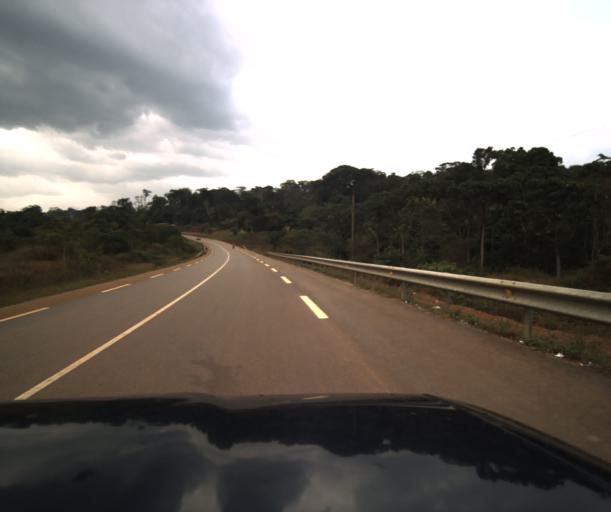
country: CM
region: Centre
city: Akono
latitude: 3.6089
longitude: 11.3149
